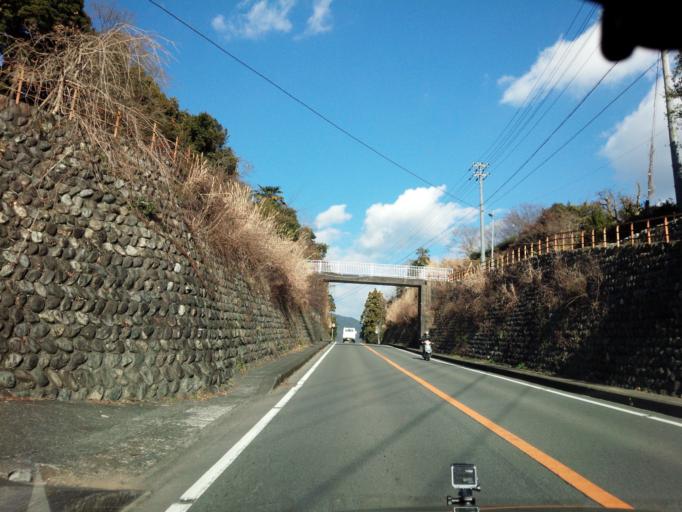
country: JP
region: Shizuoka
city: Fujinomiya
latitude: 35.1050
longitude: 138.5133
